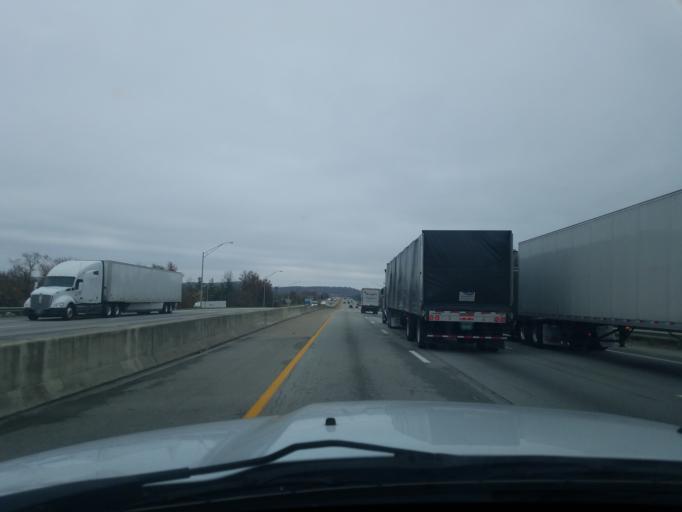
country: US
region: Kentucky
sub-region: Bullitt County
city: Shepherdsville
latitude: 37.9788
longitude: -85.6976
